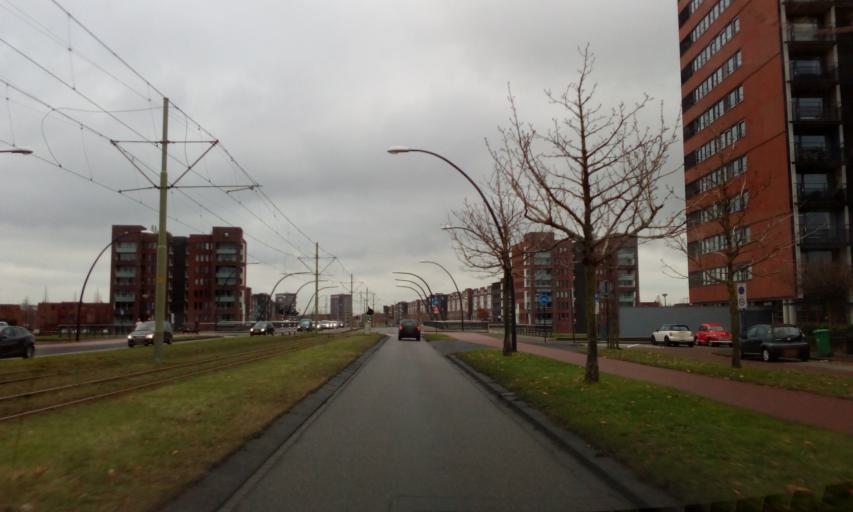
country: NL
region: South Holland
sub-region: Gemeente Rijswijk
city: Rijswijk
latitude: 52.0250
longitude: 4.2914
